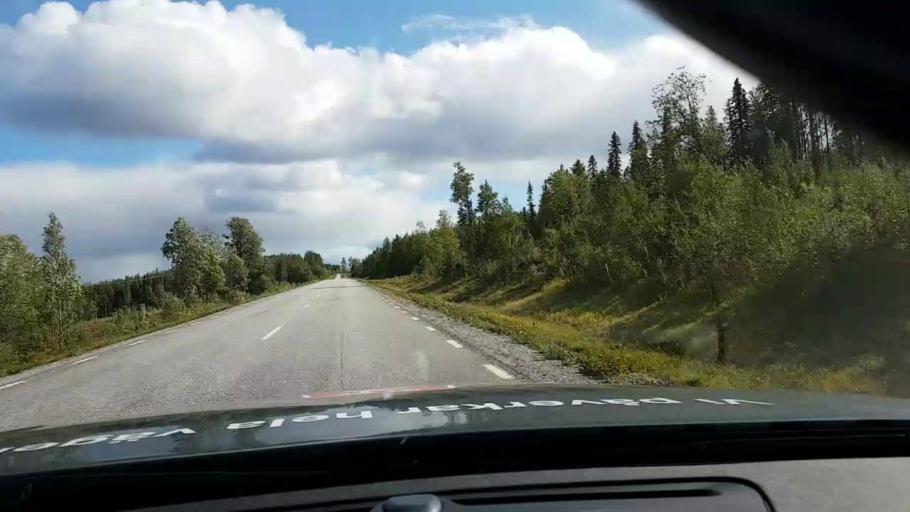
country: SE
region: Vaesterbotten
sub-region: Asele Kommun
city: Asele
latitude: 63.7771
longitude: 17.6701
